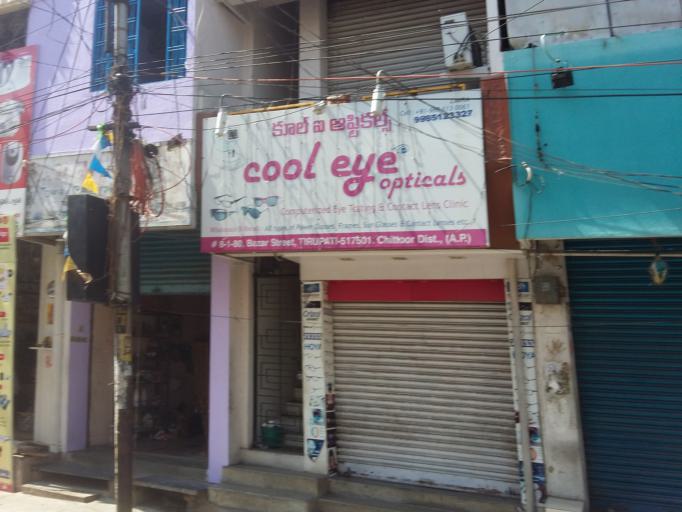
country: IN
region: Andhra Pradesh
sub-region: Chittoor
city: Tirupati
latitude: 13.6337
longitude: 79.4156
